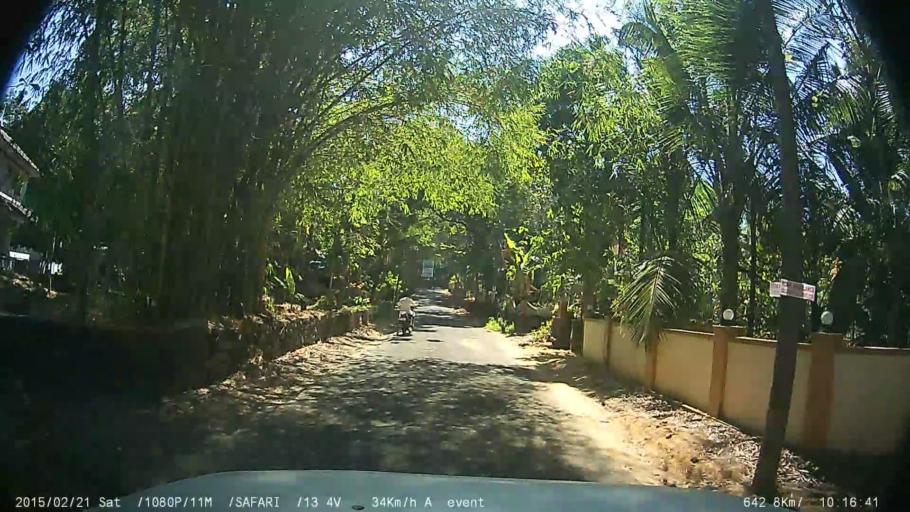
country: IN
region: Kerala
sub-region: Ernakulam
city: Muvattupuzha
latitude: 9.8810
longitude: 76.6458
